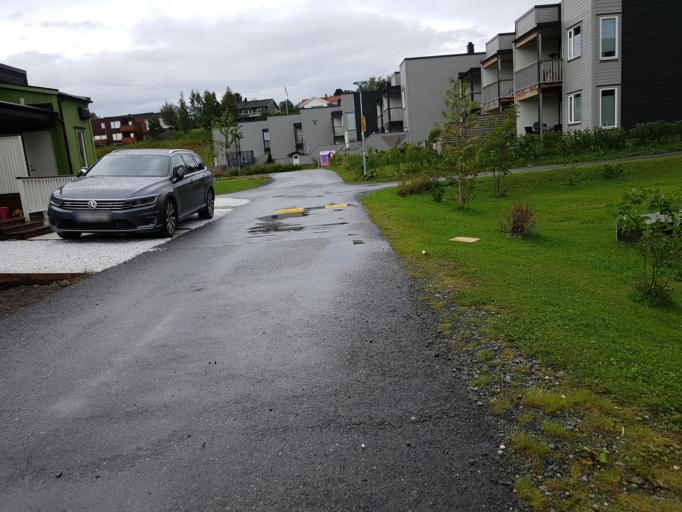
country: NO
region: Sor-Trondelag
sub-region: Trondheim
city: Trondheim
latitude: 63.3887
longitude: 10.4101
